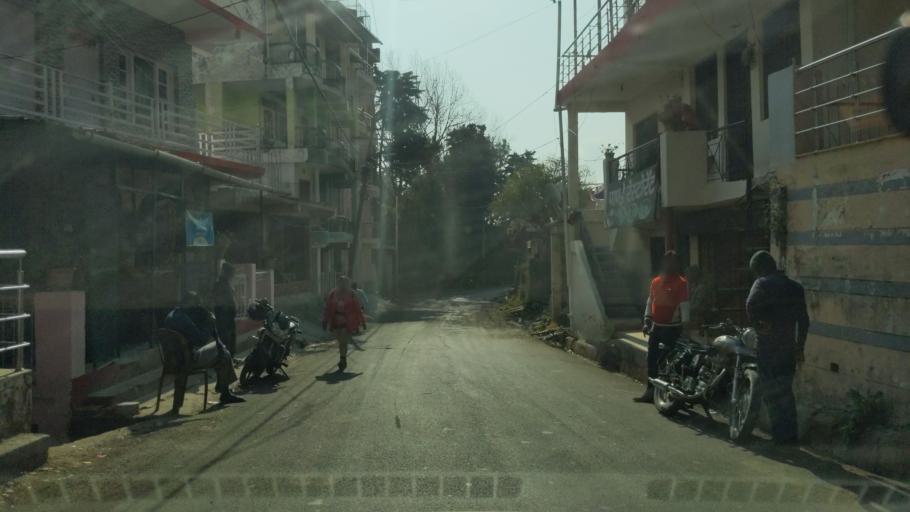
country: IN
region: Uttarakhand
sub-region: Naini Tal
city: Bhowali
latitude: 29.3860
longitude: 79.5288
